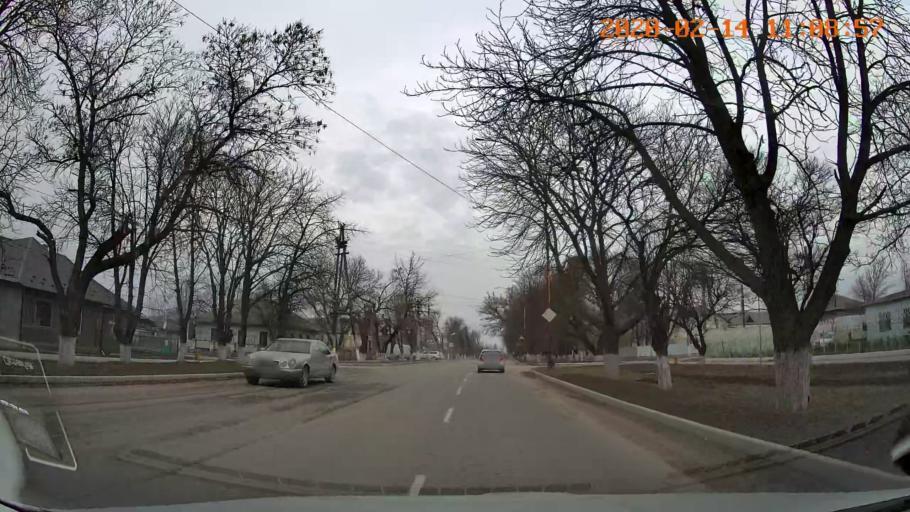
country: MD
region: Raionul Edinet
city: Edinet
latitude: 48.1751
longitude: 27.2976
